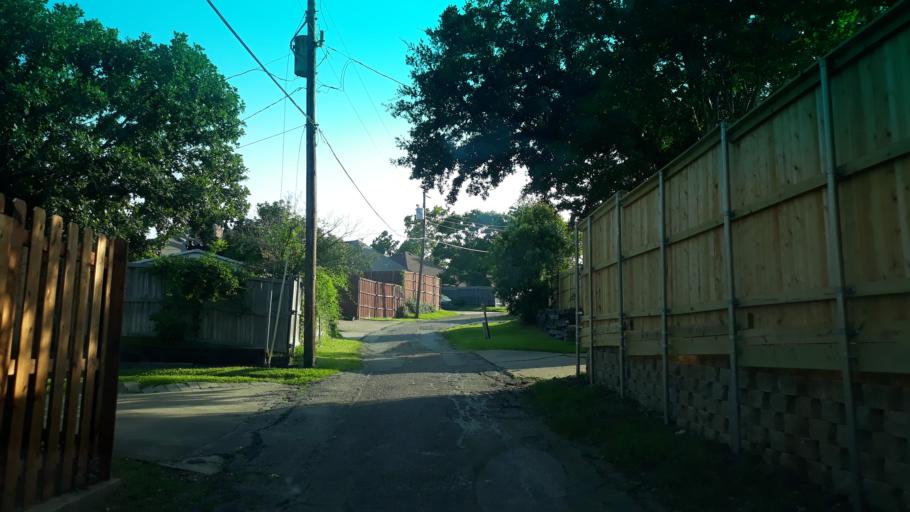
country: US
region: Texas
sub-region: Dallas County
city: Irving
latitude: 32.8531
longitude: -96.9800
